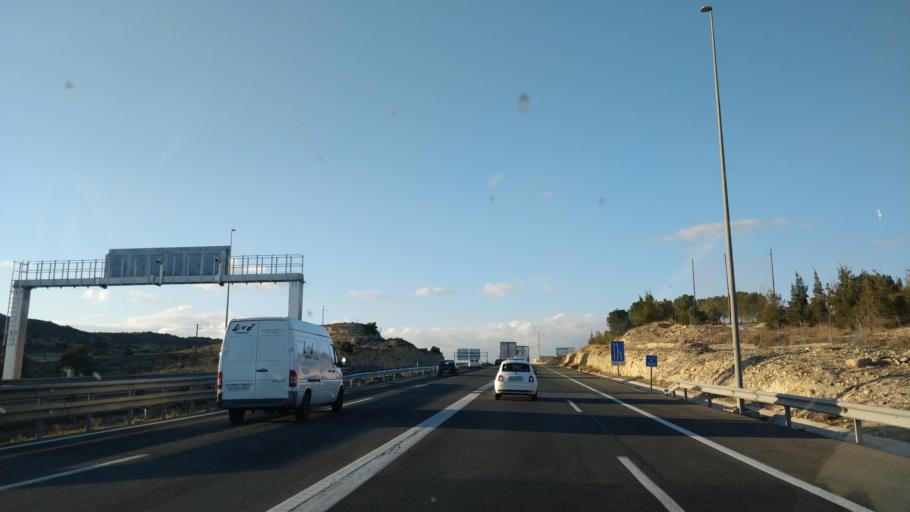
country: ES
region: Valencia
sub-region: Provincia de Alicante
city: Monforte del Cid
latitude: 38.3581
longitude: -0.6777
